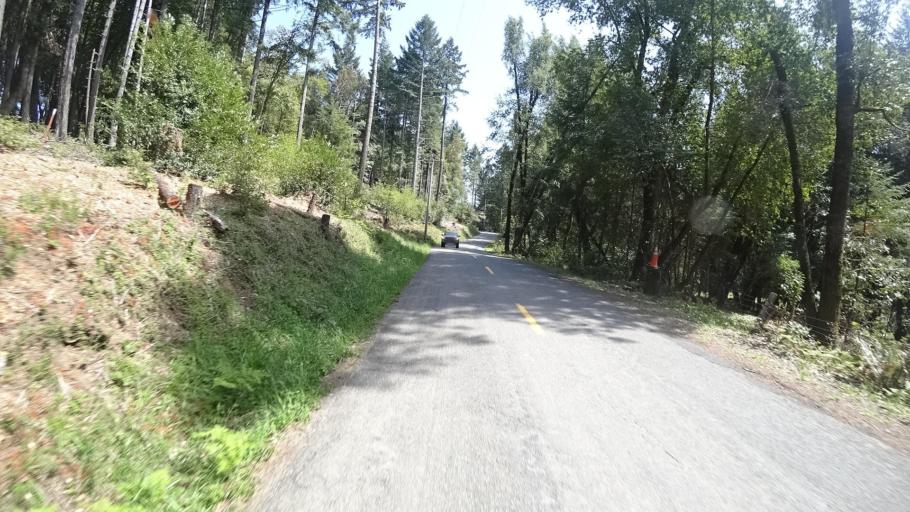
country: US
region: California
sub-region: Humboldt County
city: Redway
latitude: 40.3580
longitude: -123.7235
